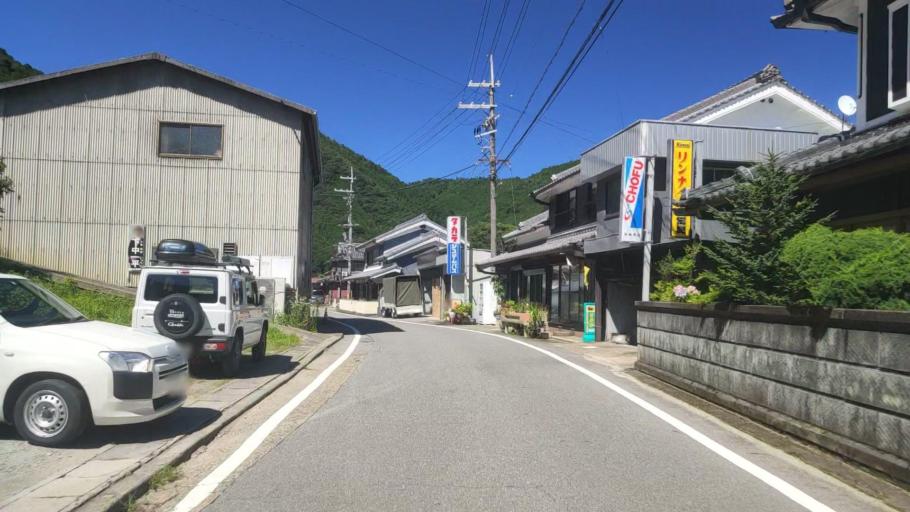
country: JP
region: Nara
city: Yoshino-cho
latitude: 34.3889
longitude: 135.9202
